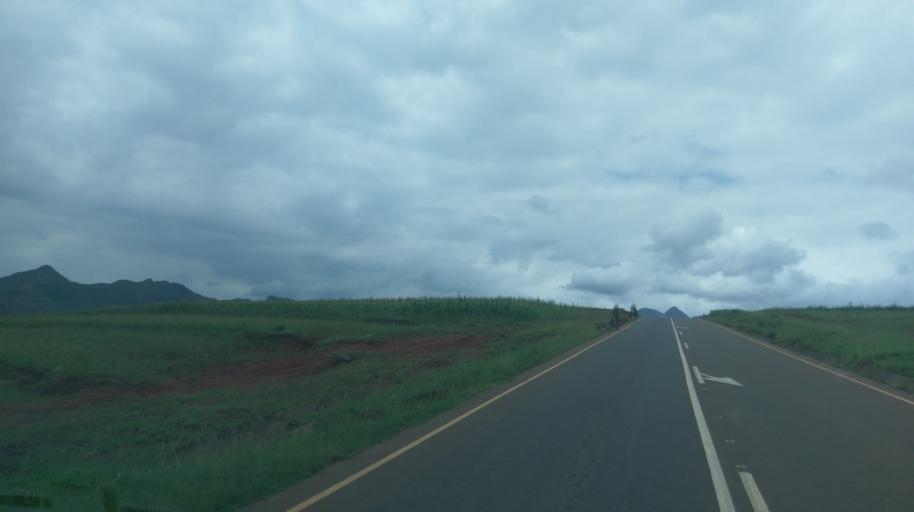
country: LS
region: Leribe
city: Leribe
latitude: -29.0328
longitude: 28.2568
